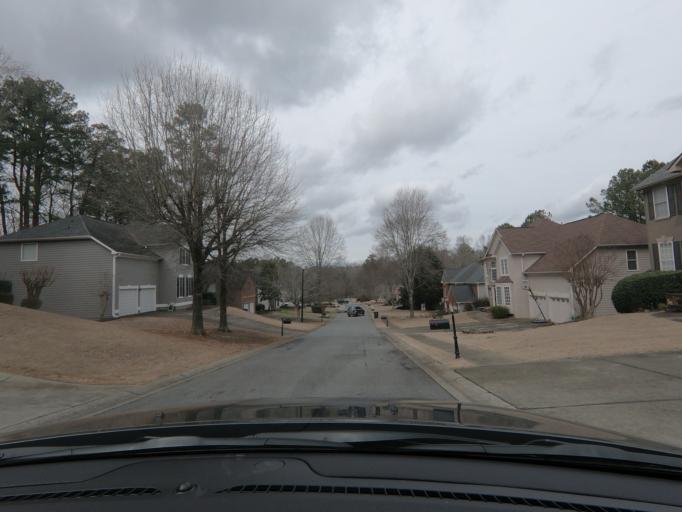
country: US
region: Georgia
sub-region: Cobb County
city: Kennesaw
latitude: 34.0489
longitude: -84.6352
